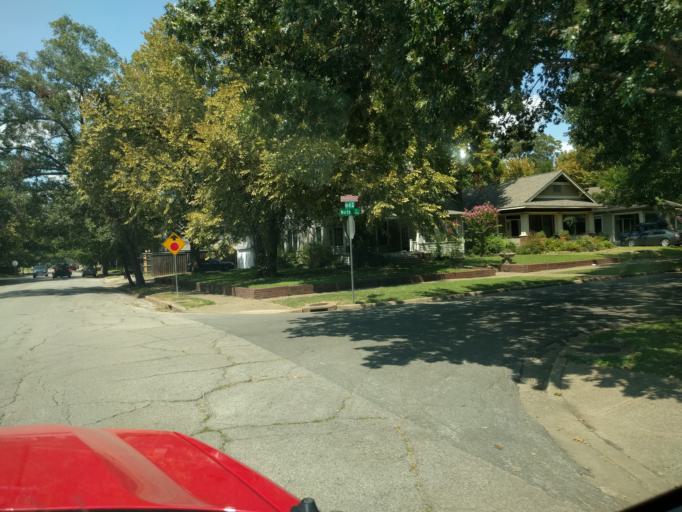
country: US
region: Texas
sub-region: Dallas County
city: Highland Park
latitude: 32.8000
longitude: -96.7658
